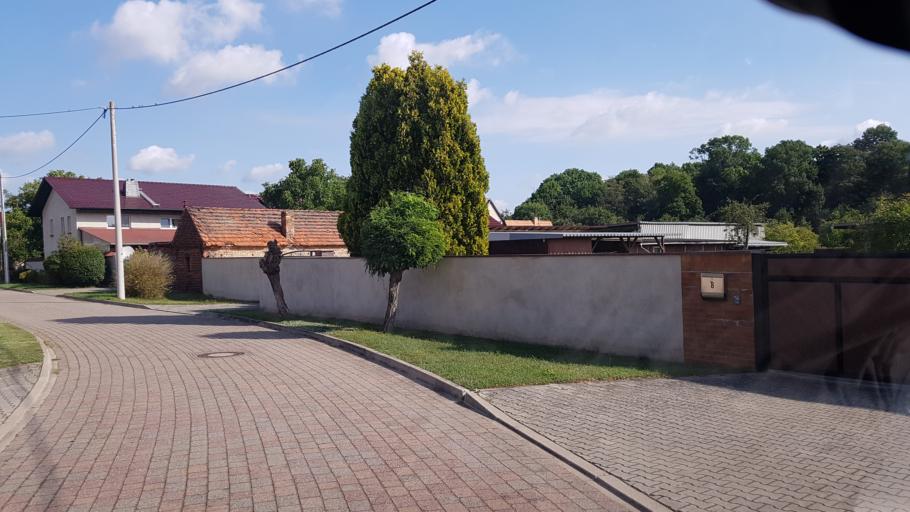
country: DE
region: Brandenburg
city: Lubbenau
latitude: 51.8852
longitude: 13.9050
